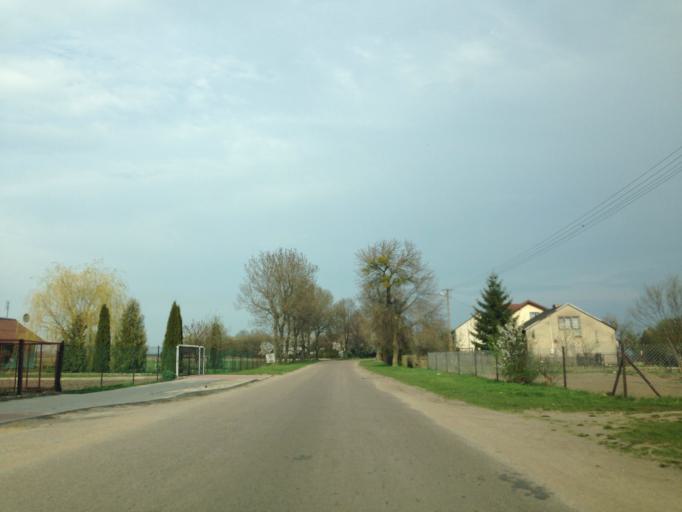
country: PL
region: Masovian Voivodeship
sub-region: Powiat zurominski
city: Siemiatkowo
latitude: 52.9639
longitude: 20.0048
